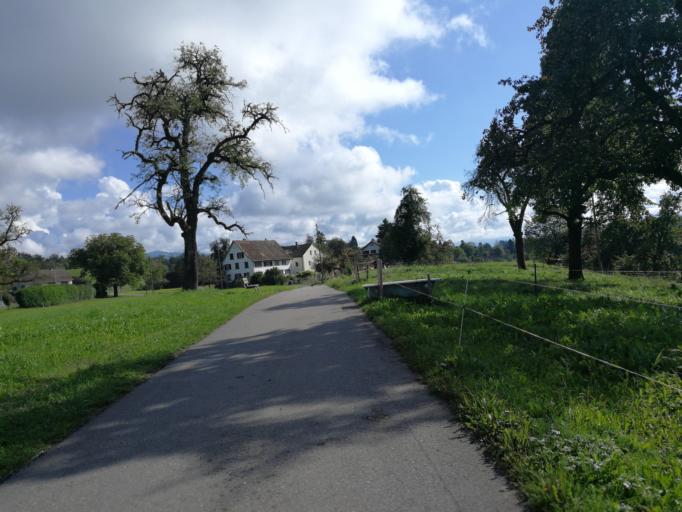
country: CH
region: Zurich
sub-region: Bezirk Meilen
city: Uerikon
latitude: 47.2424
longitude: 8.7616
